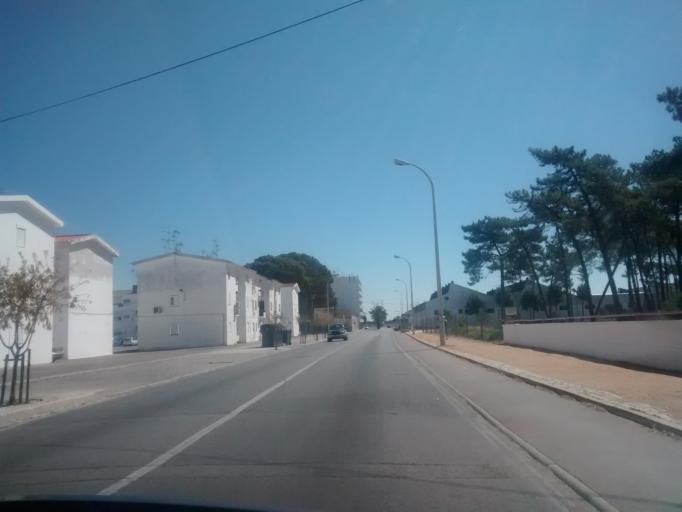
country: PT
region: Faro
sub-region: Vila Real de Santo Antonio
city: Vila Real de Santo Antonio
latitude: 37.1873
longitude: -7.4162
